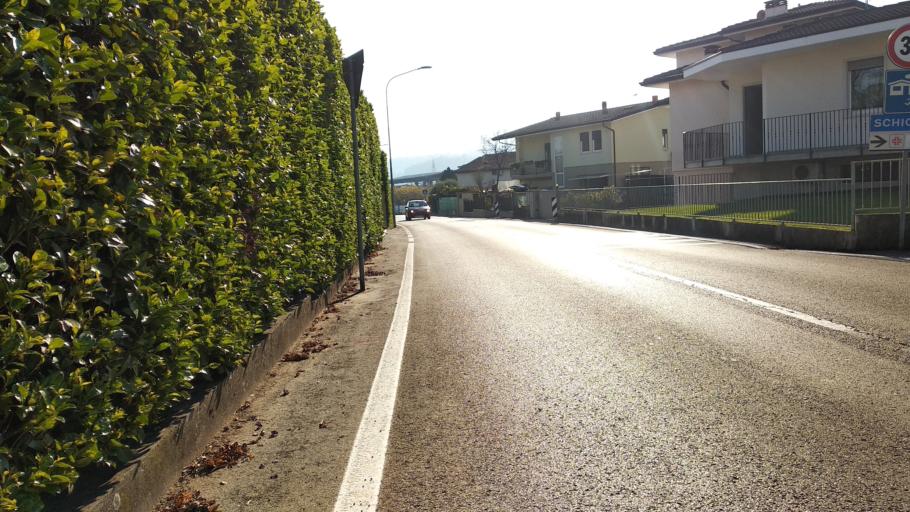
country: IT
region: Veneto
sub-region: Provincia di Vicenza
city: San Vito di Leguzzano
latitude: 45.6904
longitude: 11.3748
